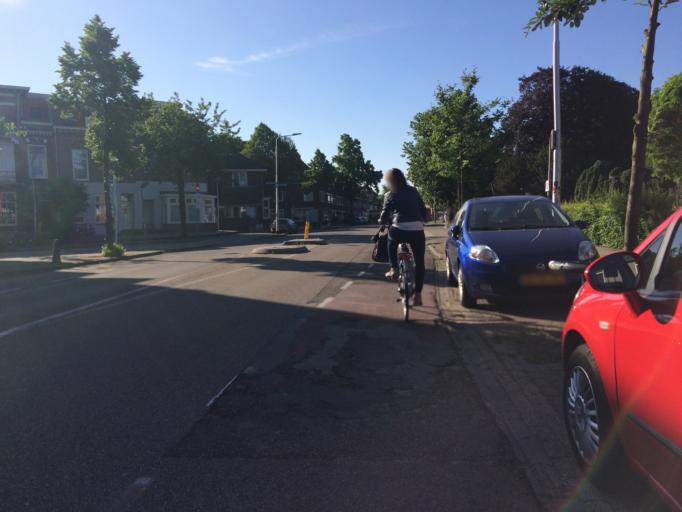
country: NL
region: Gelderland
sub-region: Gemeente Nijmegen
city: Nijmegen
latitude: 51.8402
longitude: 5.8726
